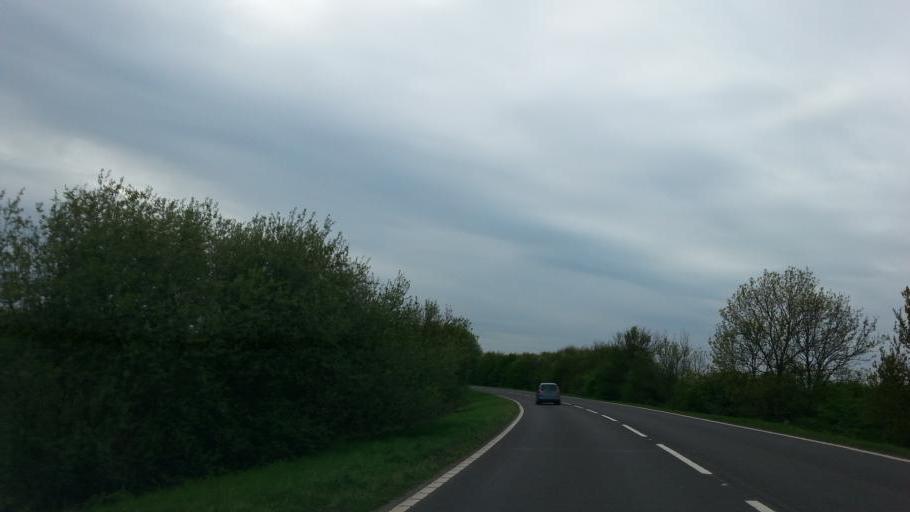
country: GB
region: England
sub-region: Cambridgeshire
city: March
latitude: 52.5204
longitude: 0.0898
